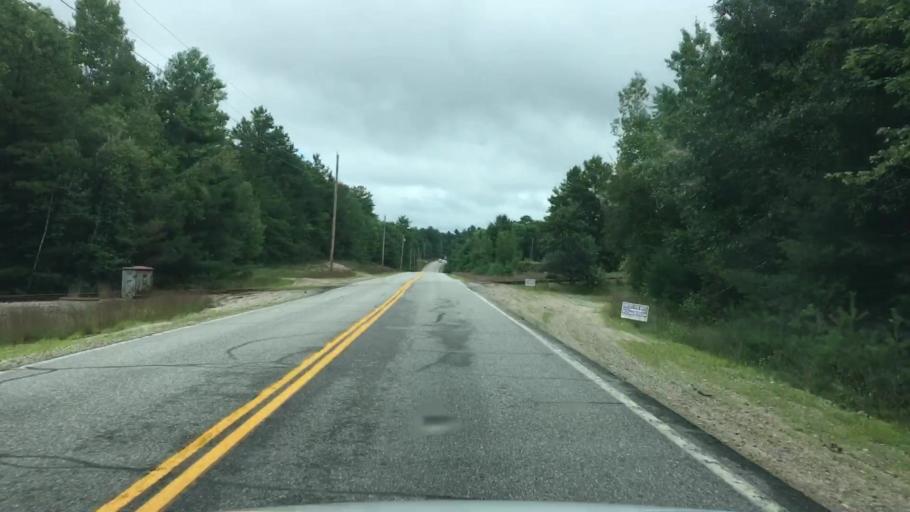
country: US
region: Maine
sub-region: Oxford County
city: Hiram
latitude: 43.8996
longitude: -70.8351
